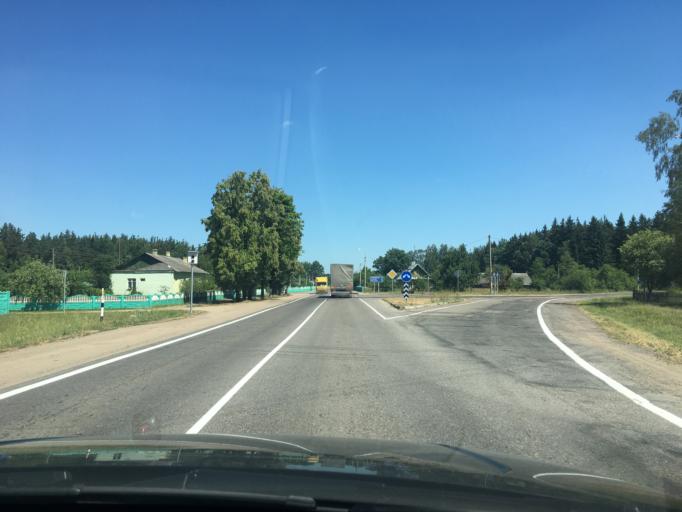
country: BY
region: Grodnenskaya
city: Iwye
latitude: 54.0254
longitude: 25.9194
